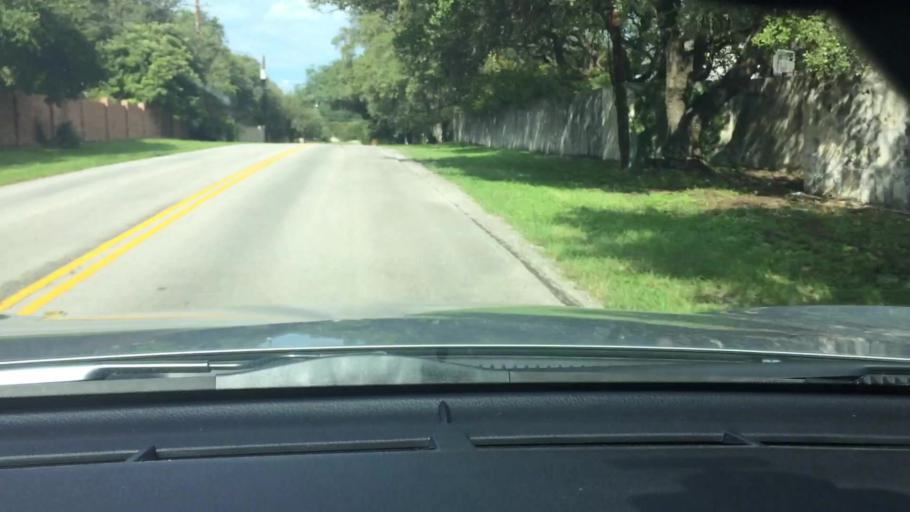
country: US
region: Texas
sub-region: Bexar County
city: Shavano Park
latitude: 29.5600
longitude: -98.5564
